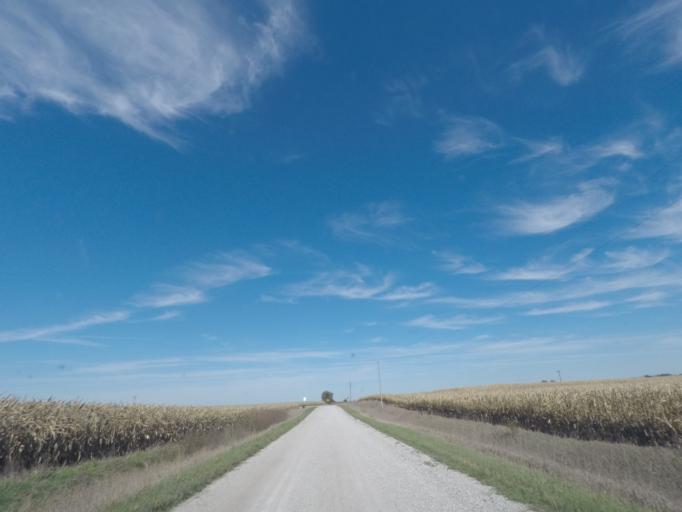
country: US
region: Iowa
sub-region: Story County
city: Nevada
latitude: 42.0212
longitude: -93.3573
